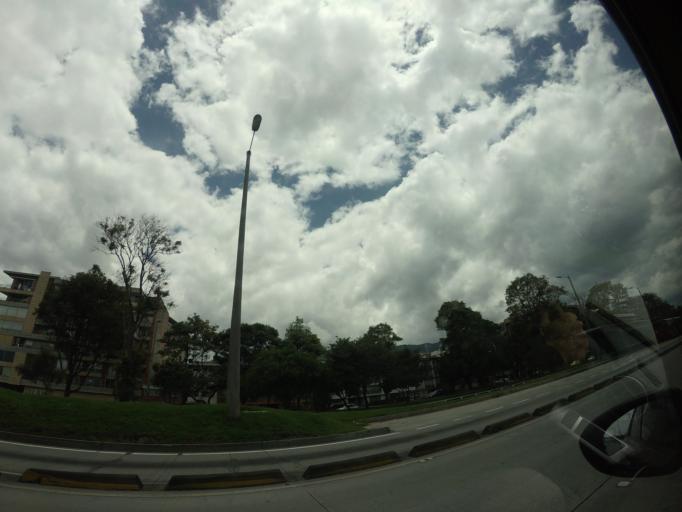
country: CO
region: Bogota D.C.
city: Barrio San Luis
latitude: 4.6742
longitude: -74.0594
